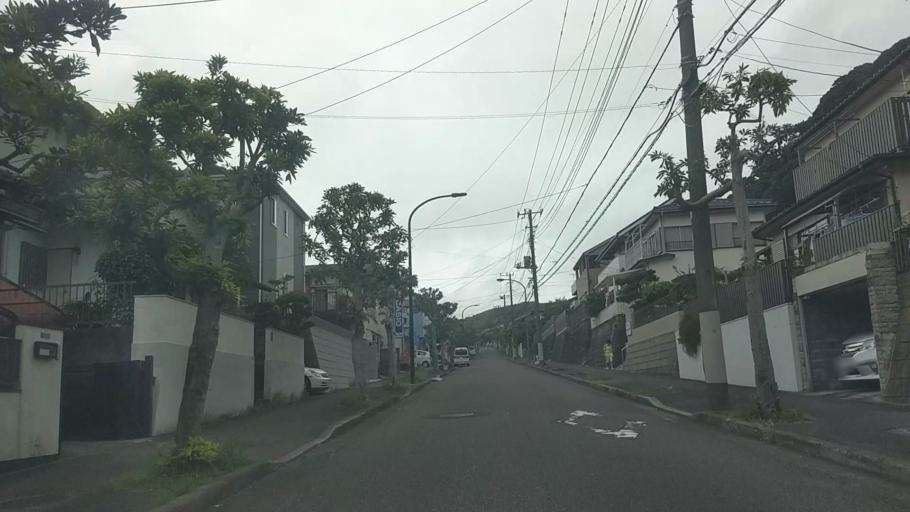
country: JP
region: Kanagawa
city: Yokosuka
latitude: 35.2533
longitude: 139.7368
